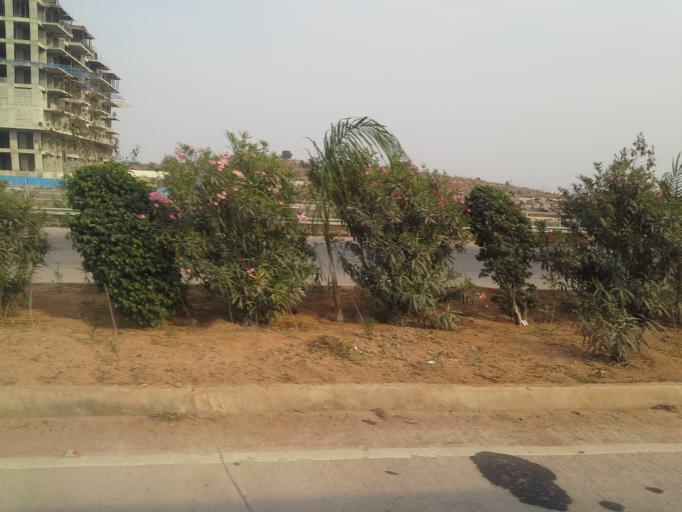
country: IN
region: Telangana
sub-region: Rangareddi
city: Kukatpalli
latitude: 17.4049
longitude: 78.3534
